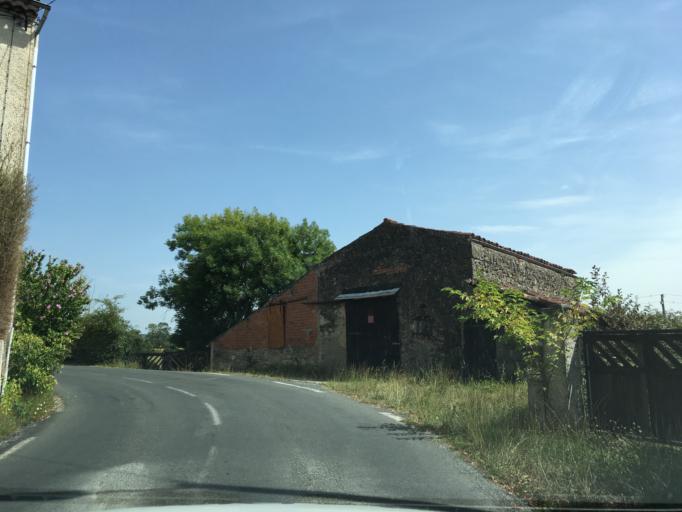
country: FR
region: Midi-Pyrenees
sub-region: Departement du Tarn
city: Castres
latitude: 43.6343
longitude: 2.2290
